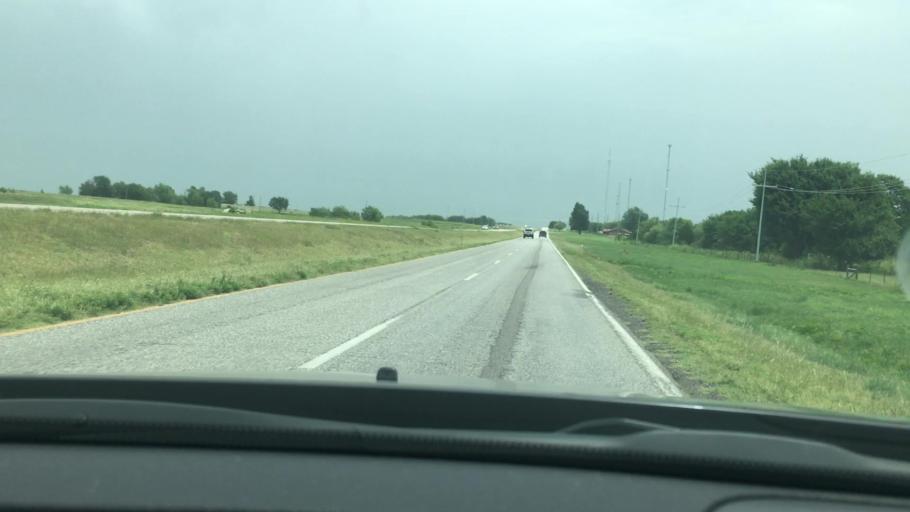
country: US
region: Oklahoma
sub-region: Pontotoc County
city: Ada
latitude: 34.6761
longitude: -96.7738
